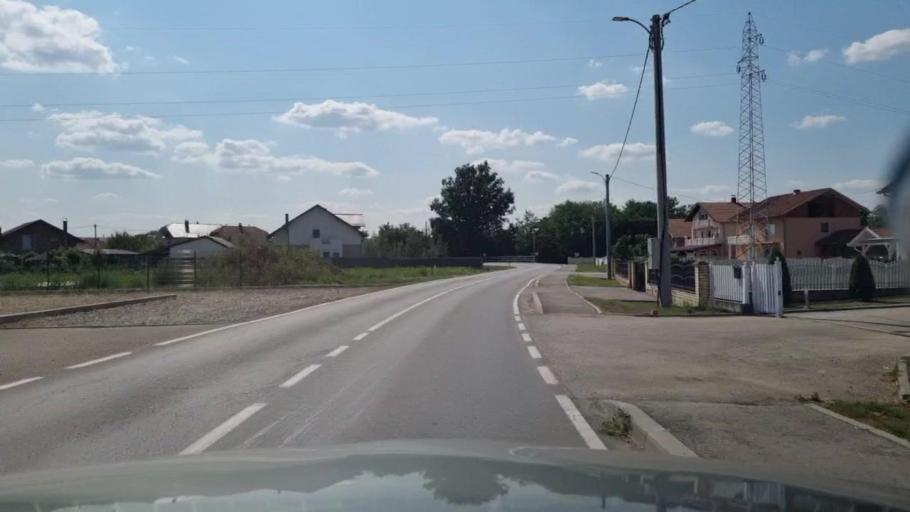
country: BA
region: Federation of Bosnia and Herzegovina
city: Odzak
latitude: 45.0217
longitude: 18.3368
